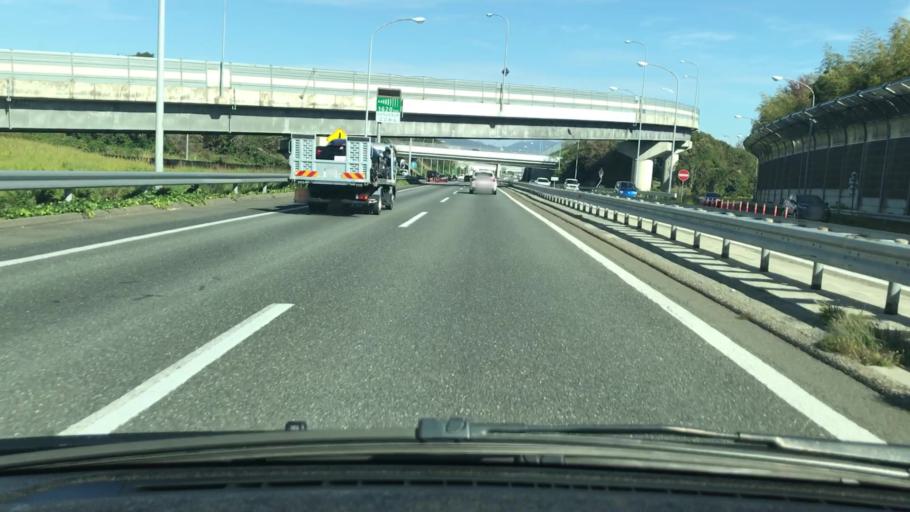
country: JP
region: Osaka
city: Ibaraki
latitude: 34.8023
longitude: 135.5410
